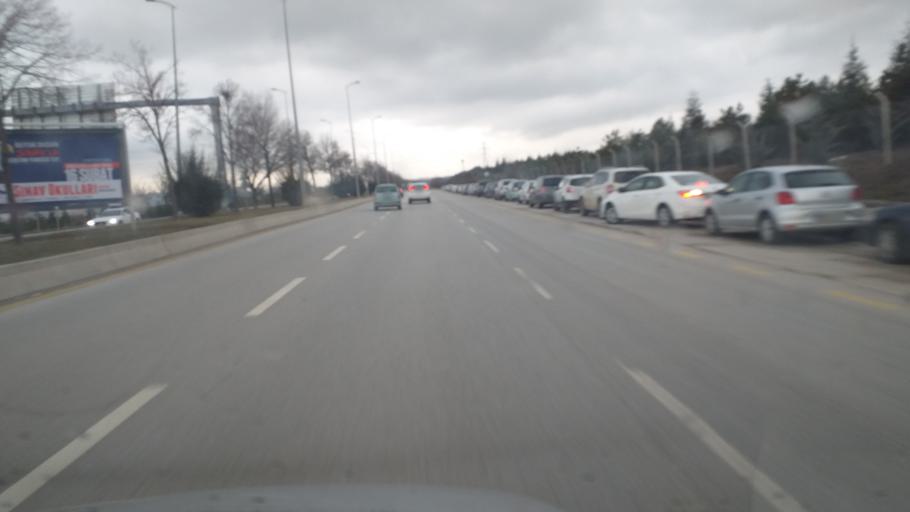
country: TR
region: Ankara
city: Batikent
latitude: 39.9040
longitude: 32.7327
